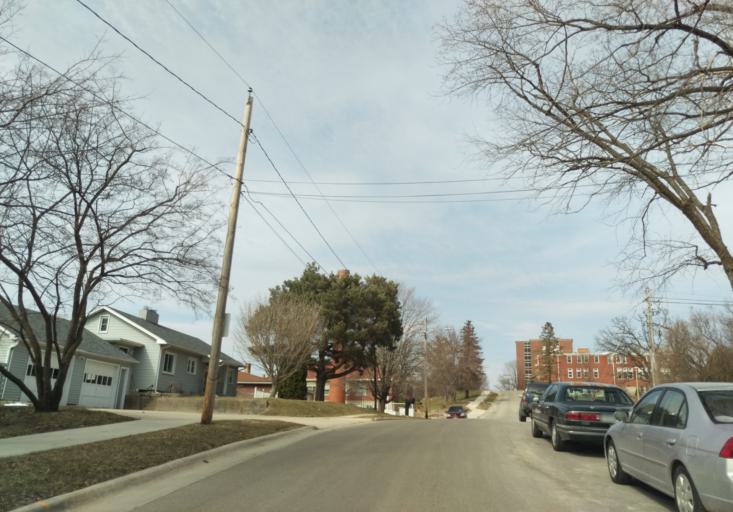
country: US
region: Iowa
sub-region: Winneshiek County
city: Decorah
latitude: 43.3088
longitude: -91.8067
